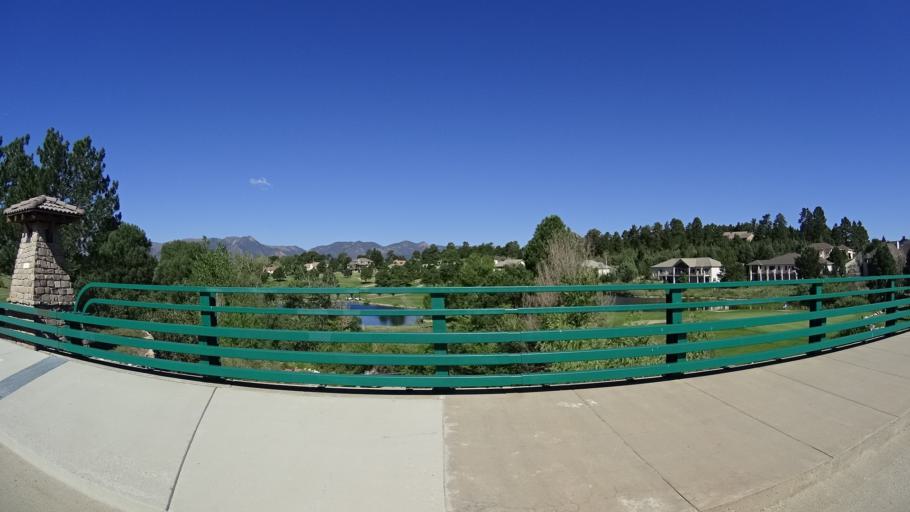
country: US
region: Colorado
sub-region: El Paso County
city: Air Force Academy
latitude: 38.9709
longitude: -104.7854
